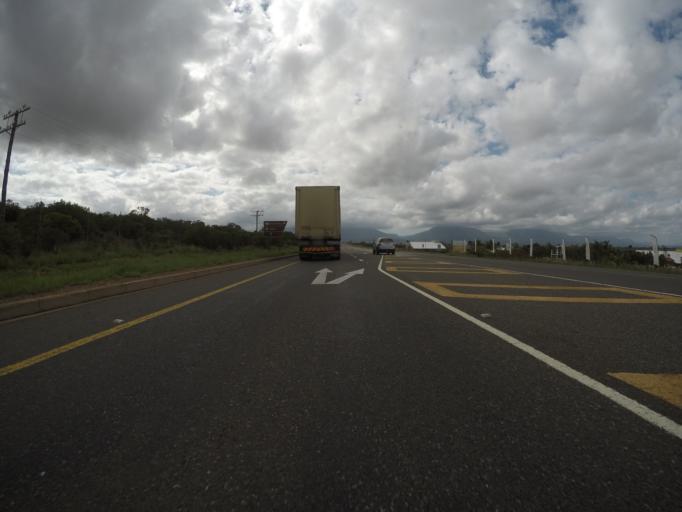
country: ZA
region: Western Cape
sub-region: Eden District Municipality
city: Riversdale
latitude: -34.1118
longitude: 21.2539
